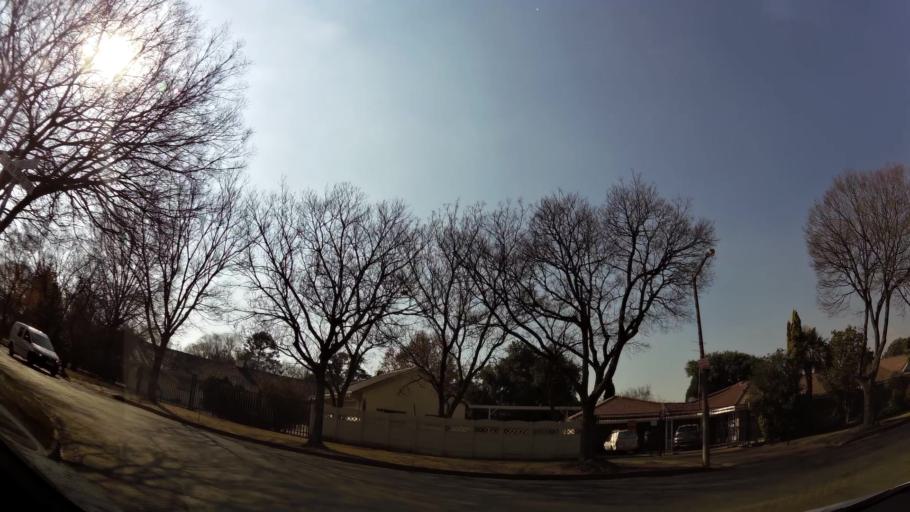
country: ZA
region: Gauteng
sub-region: Ekurhuleni Metropolitan Municipality
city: Boksburg
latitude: -26.1816
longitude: 28.2690
